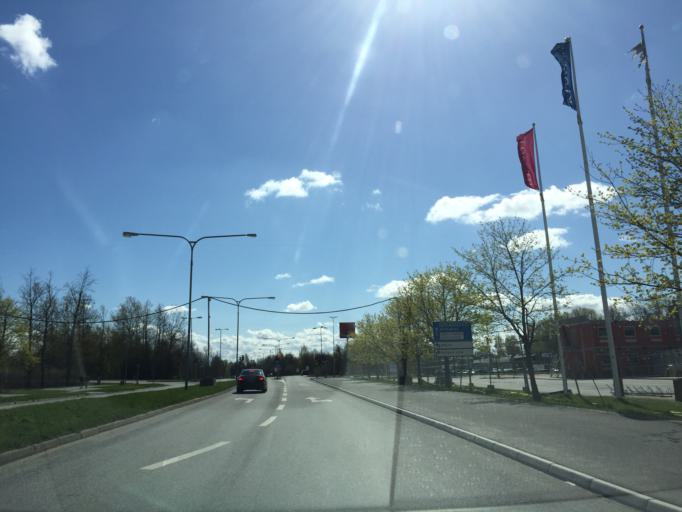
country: SE
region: OErebro
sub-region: Orebro Kommun
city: Orebro
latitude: 59.2712
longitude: 15.1745
